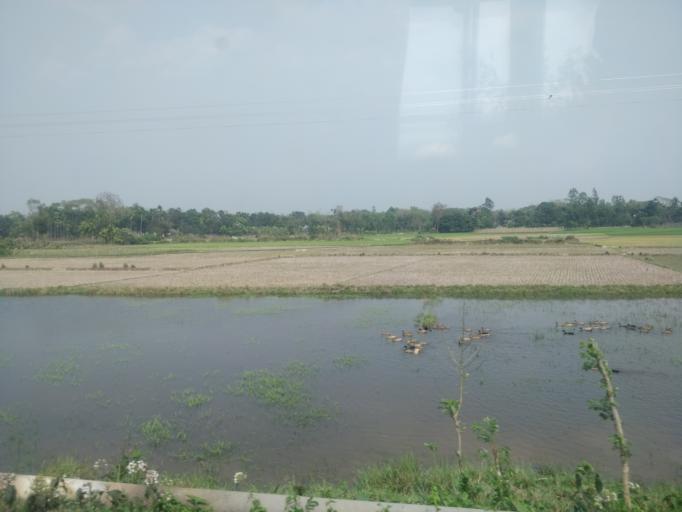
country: BD
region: Sylhet
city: Habiganj
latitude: 24.3212
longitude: 91.4346
